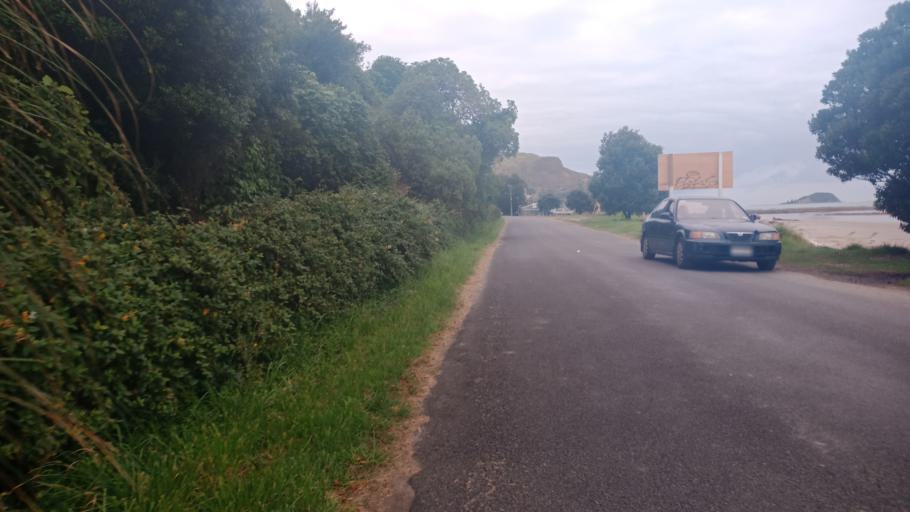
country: NZ
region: Gisborne
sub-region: Gisborne District
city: Gisborne
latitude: -38.6809
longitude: 178.0284
